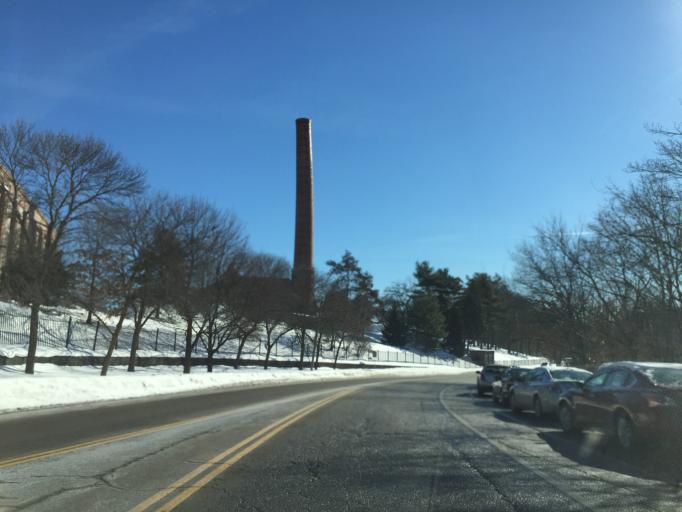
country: US
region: Massachusetts
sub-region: Middlesex County
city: Watertown
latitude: 42.3621
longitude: -71.1669
